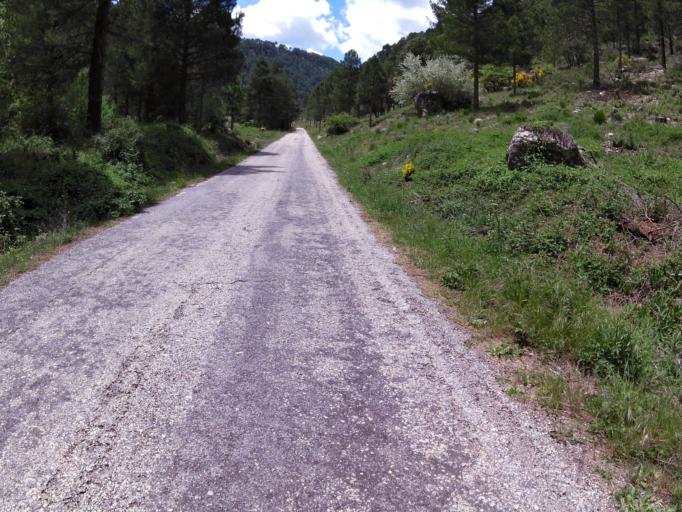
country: ES
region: Castille-La Mancha
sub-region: Provincia de Albacete
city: Paterna del Madera
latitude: 38.5743
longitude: -2.3546
